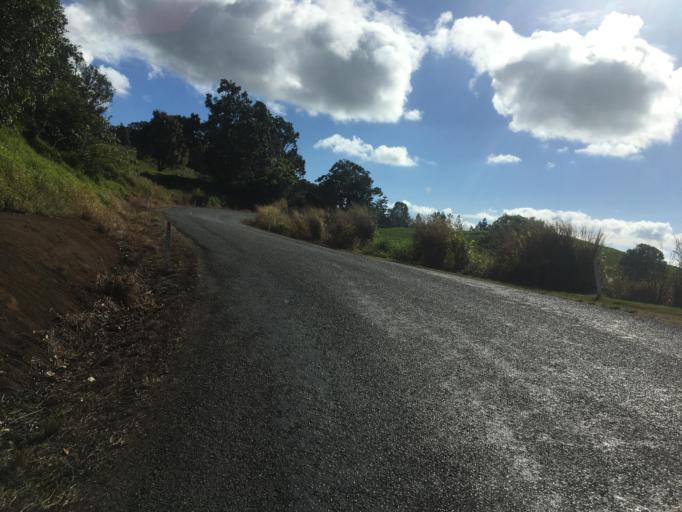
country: AU
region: Queensland
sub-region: Tablelands
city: Ravenshoe
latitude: -17.5204
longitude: 145.6098
